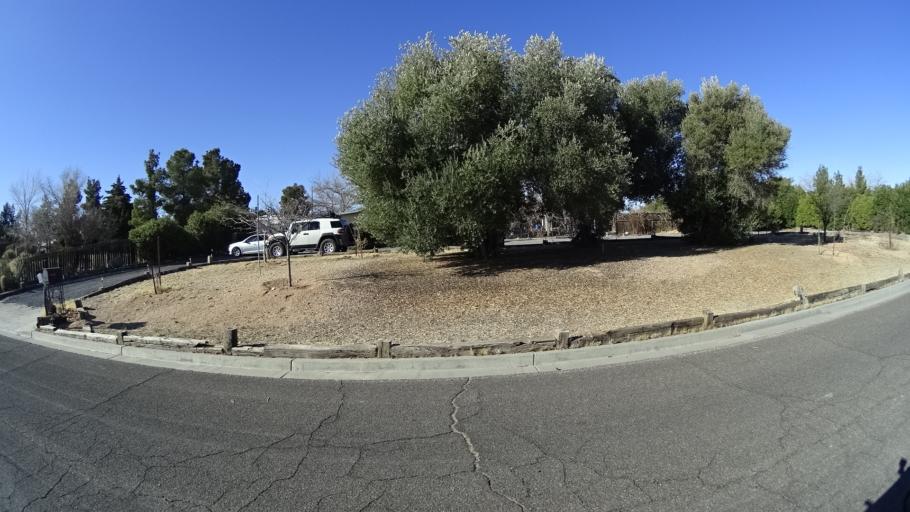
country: US
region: Arizona
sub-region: Mohave County
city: Kingman
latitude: 35.2018
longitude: -114.0062
